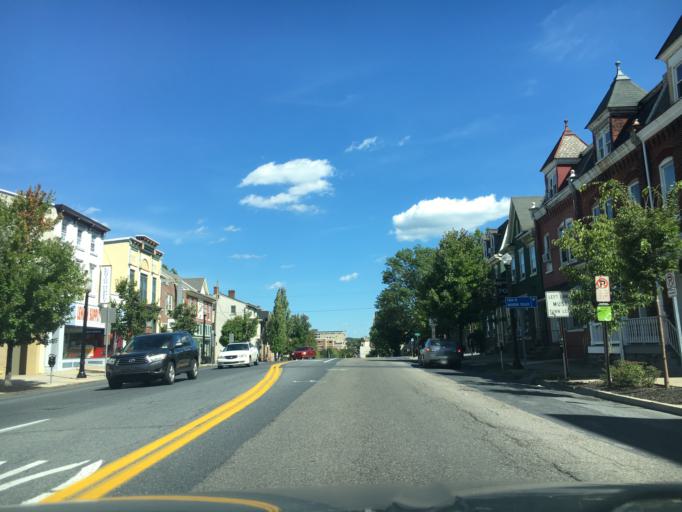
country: US
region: Pennsylvania
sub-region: Northampton County
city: Bethlehem
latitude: 40.6224
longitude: -75.3878
